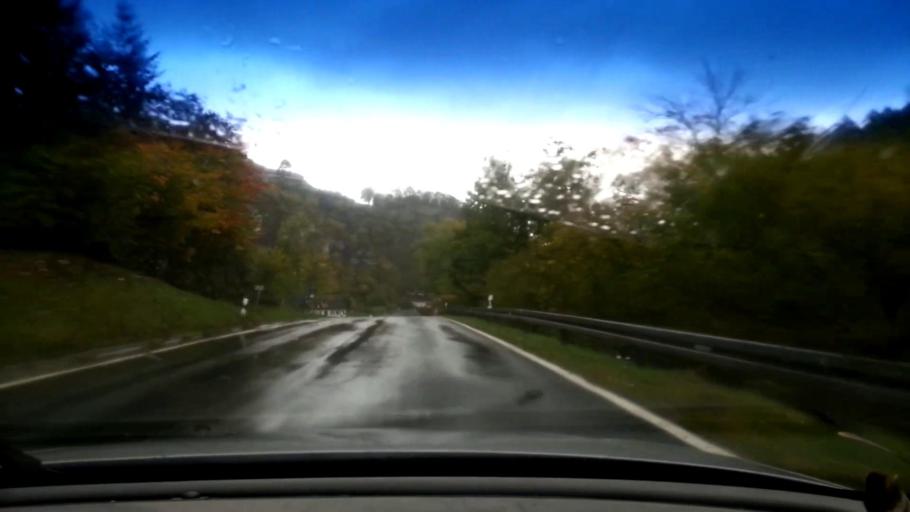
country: DE
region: Bavaria
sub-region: Upper Franconia
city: Stadelhofen
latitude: 50.0408
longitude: 11.2141
